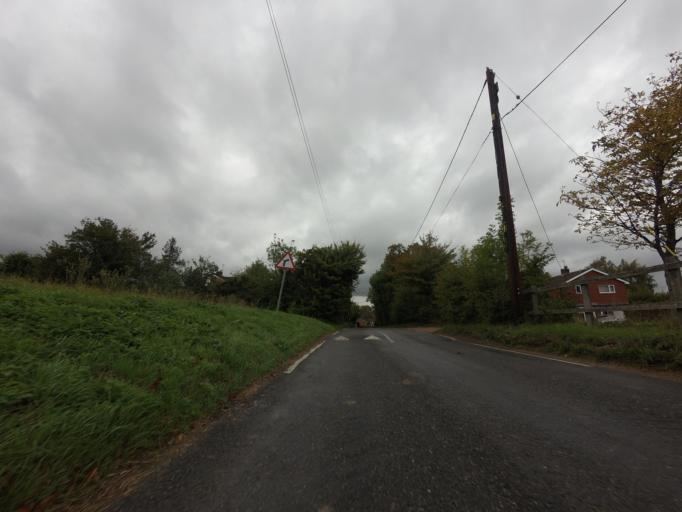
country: GB
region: England
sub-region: Cambridgeshire
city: Wimpole
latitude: 52.1767
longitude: -0.0314
